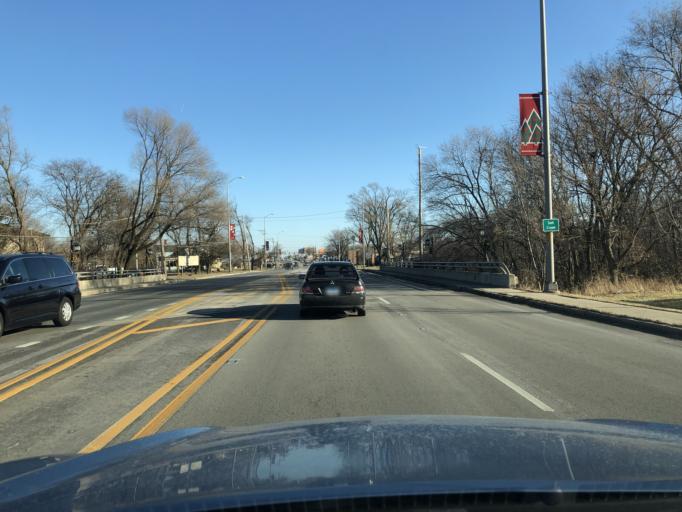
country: US
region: Illinois
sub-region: DuPage County
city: Wood Dale
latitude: 41.9644
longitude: -87.9850
